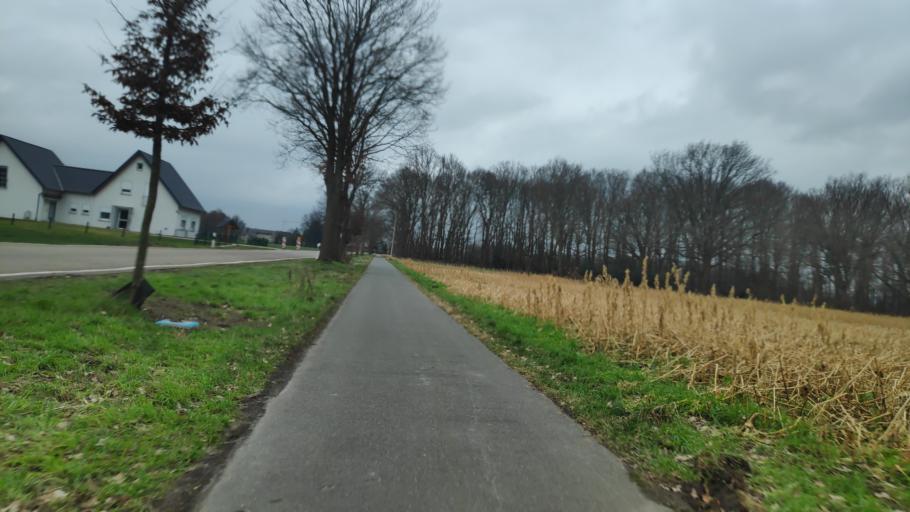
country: DE
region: North Rhine-Westphalia
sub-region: Regierungsbezirk Detmold
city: Hille
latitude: 52.3568
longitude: 8.7840
